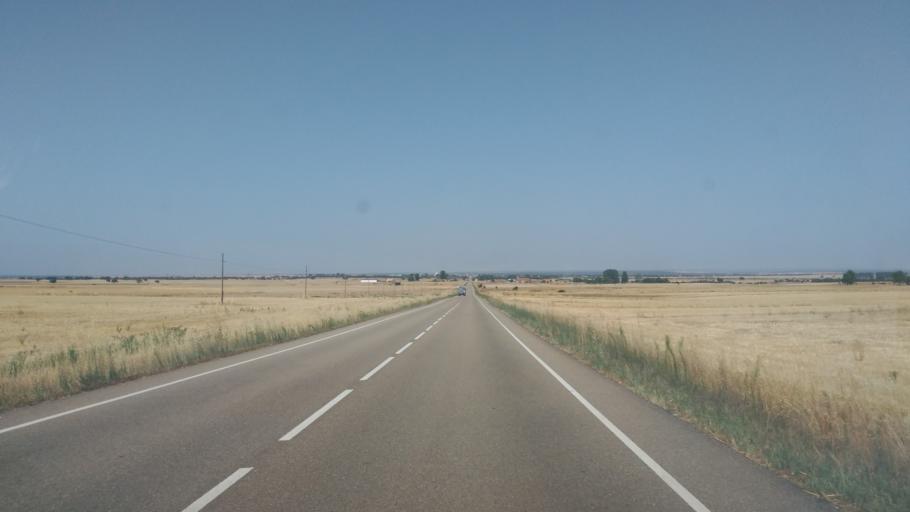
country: ES
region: Castille and Leon
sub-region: Provincia de Salamanca
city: Cabrillas
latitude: 40.7652
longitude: -6.2180
